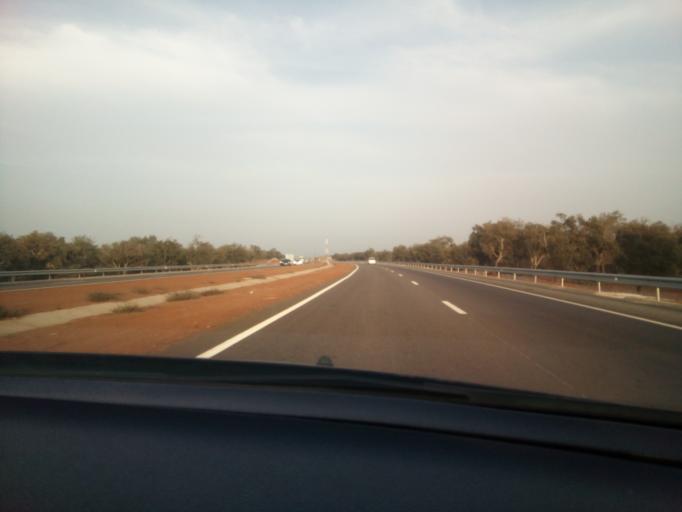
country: MA
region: Rabat-Sale-Zemmour-Zaer
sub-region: Skhirate-Temara
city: Temara
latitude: 33.8380
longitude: -6.8748
